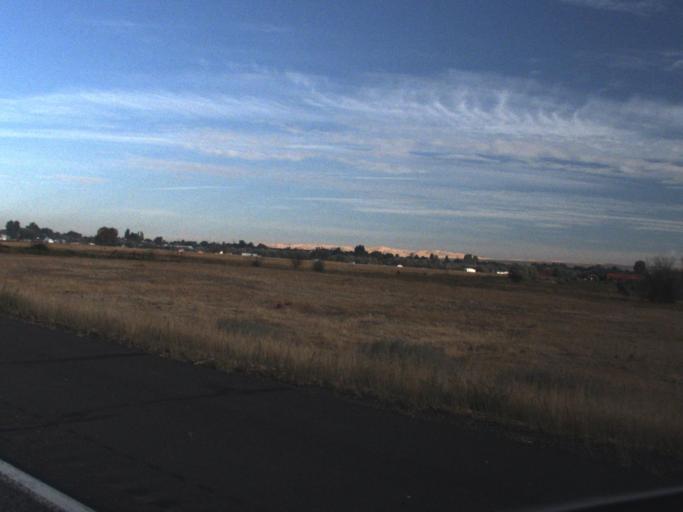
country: US
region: Washington
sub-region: Benton County
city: Prosser
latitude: 46.2197
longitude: -119.7508
